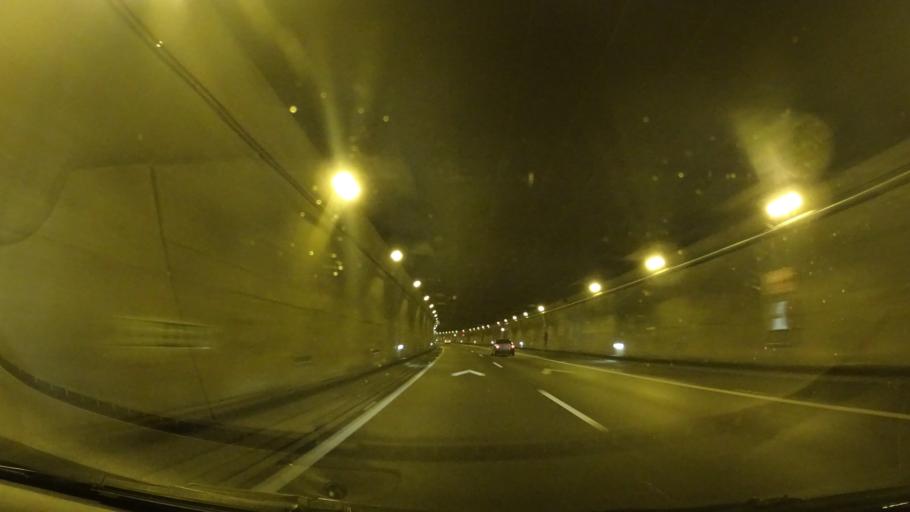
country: ES
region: Madrid
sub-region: Provincia de Madrid
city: Guadarrama
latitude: 40.7167
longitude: -4.1564
